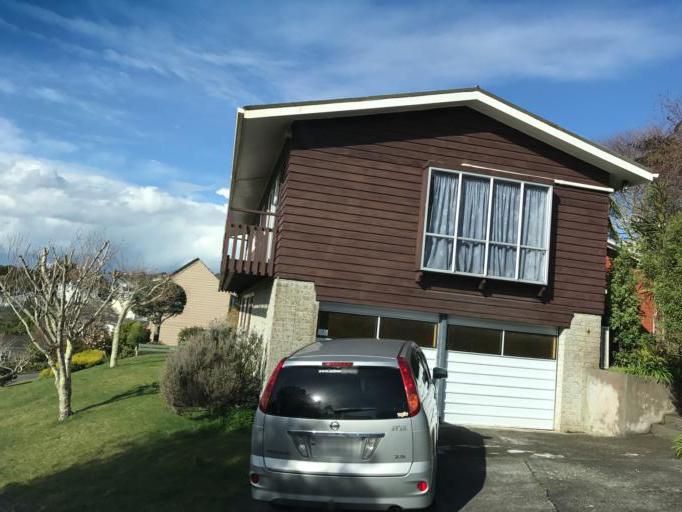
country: NZ
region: Wellington
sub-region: Wellington City
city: Kelburn
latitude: -41.2878
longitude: 174.7343
